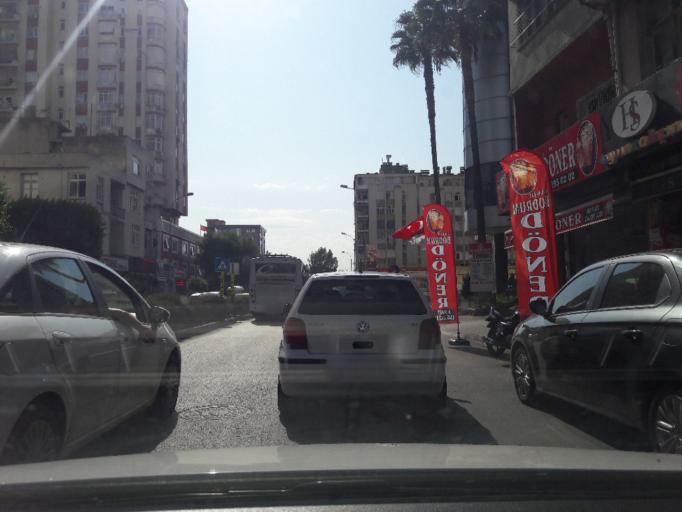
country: TR
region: Adana
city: Adana
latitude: 37.0084
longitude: 35.3241
